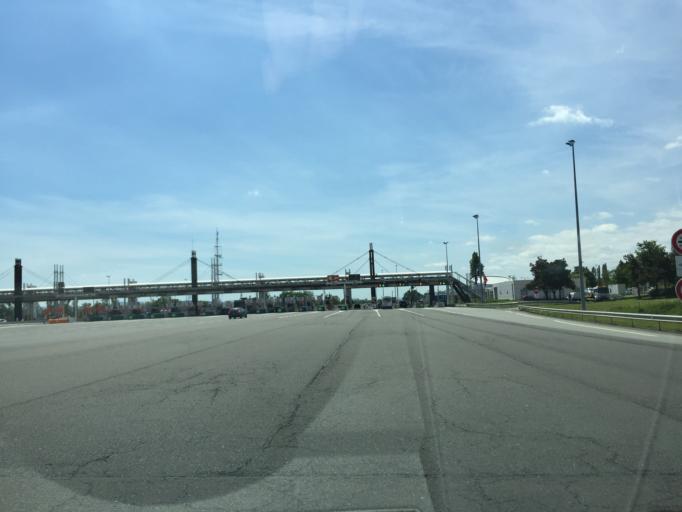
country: FR
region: Auvergne
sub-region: Departement du Puy-de-Dome
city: Gerzat
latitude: 45.8427
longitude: 3.1604
